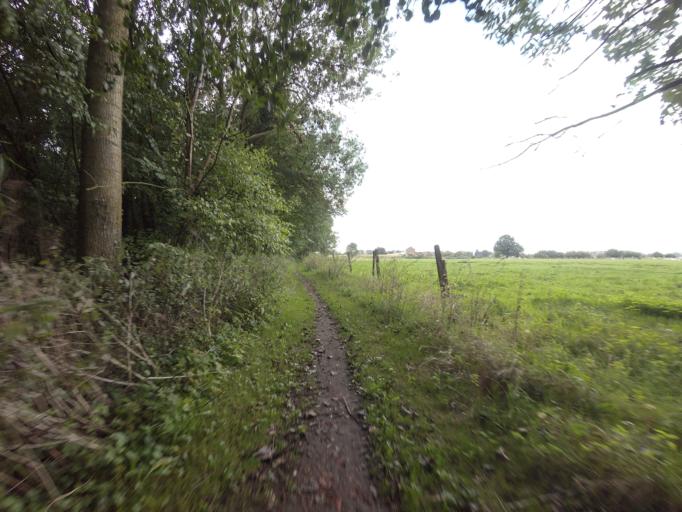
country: BE
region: Flanders
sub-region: Provincie Vlaams-Brabant
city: Kapelle-op-den-Bos
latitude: 51.0210
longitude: 4.3438
